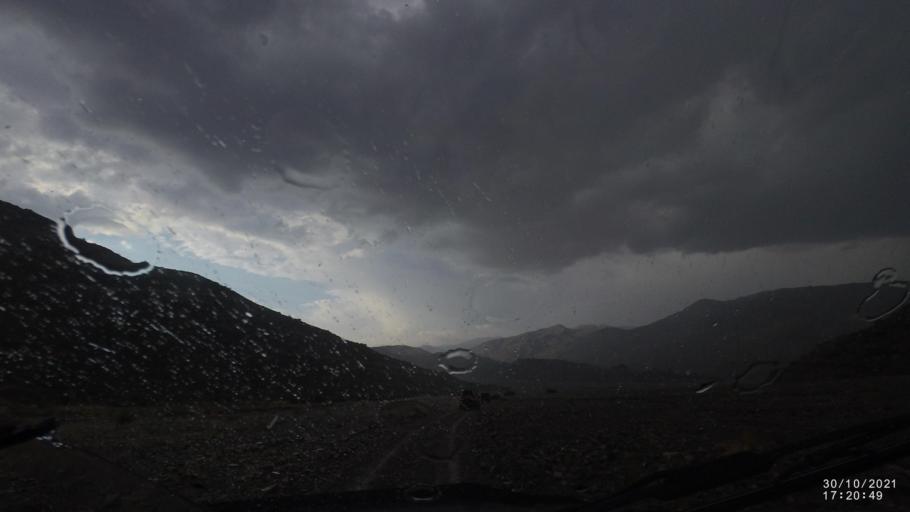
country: BO
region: Cochabamba
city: Colchani
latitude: -17.5299
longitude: -66.6195
